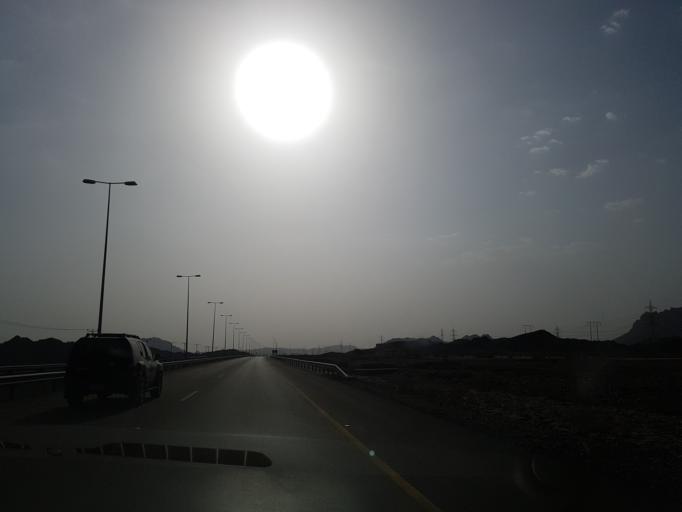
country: OM
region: Al Buraimi
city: Al Buraymi
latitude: 24.2470
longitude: 56.0267
